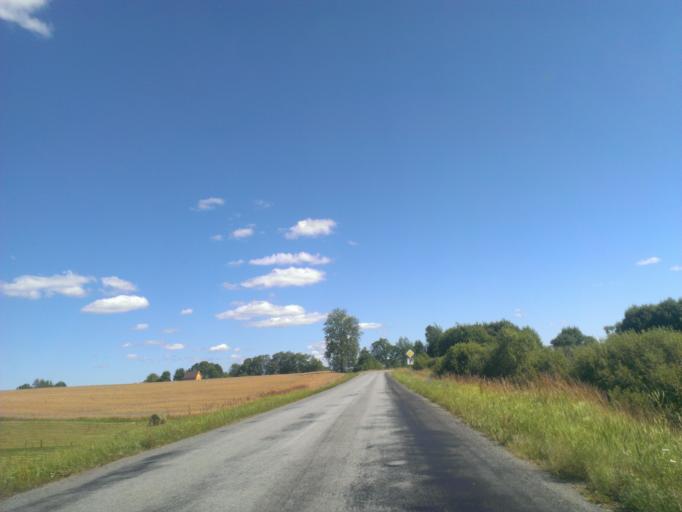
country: LV
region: Malpils
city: Malpils
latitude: 57.0141
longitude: 24.8833
